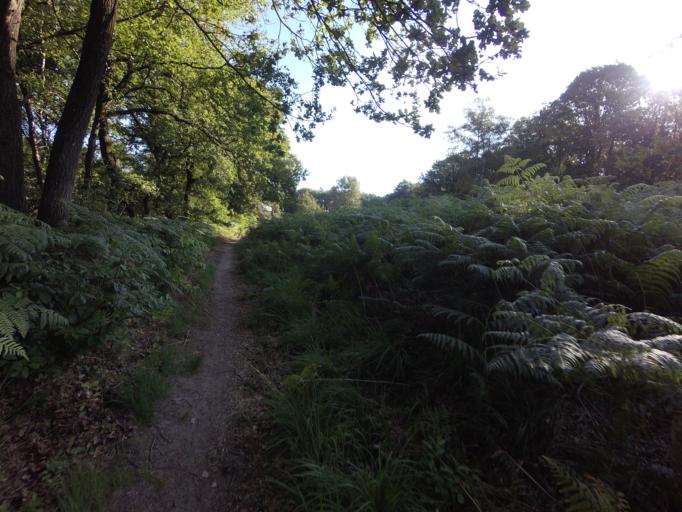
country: NL
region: Limburg
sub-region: Gemeente Roerdalen
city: Herkenbosch
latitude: 51.1767
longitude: 6.1151
